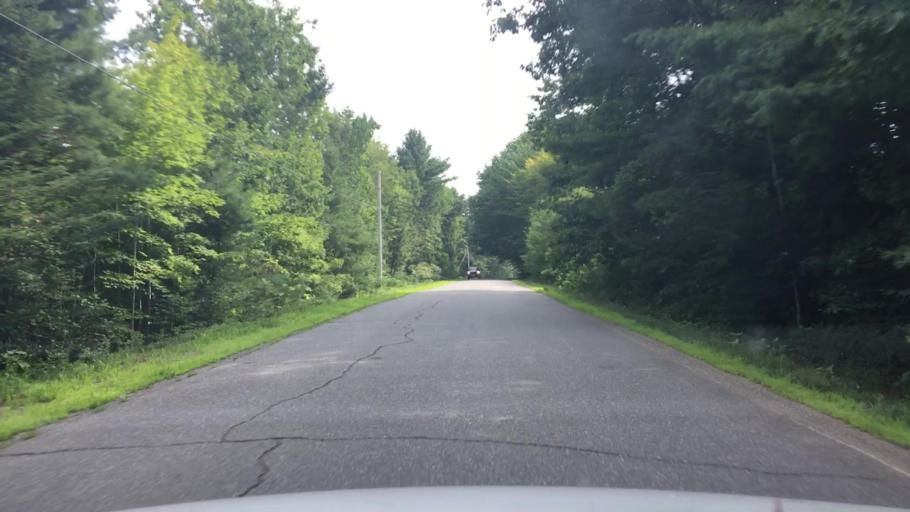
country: US
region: Maine
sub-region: Lincoln County
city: Jefferson
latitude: 44.2287
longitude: -69.4451
